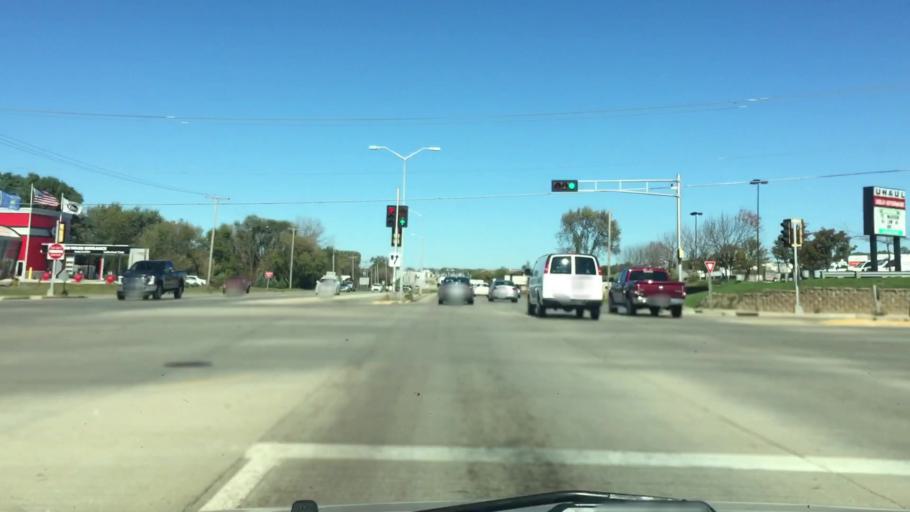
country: US
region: Wisconsin
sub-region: Waukesha County
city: Waukesha
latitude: 43.0138
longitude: -88.2004
